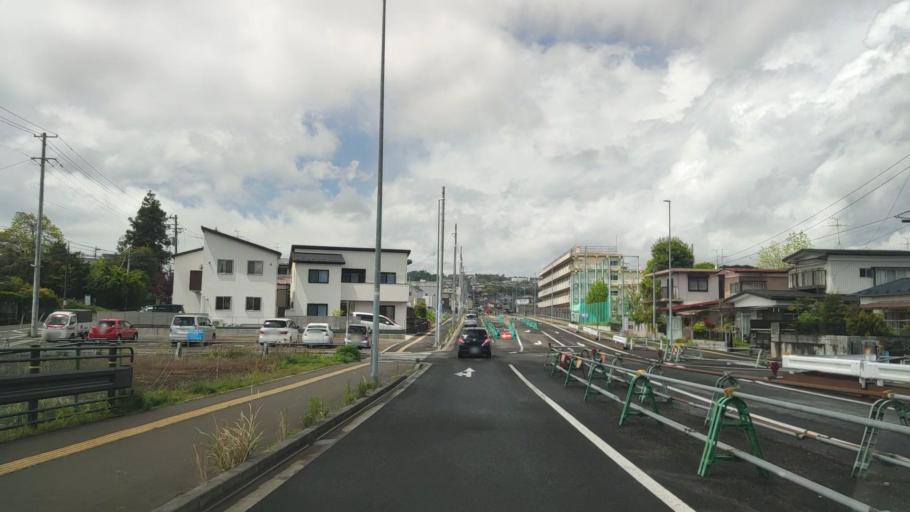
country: JP
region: Miyagi
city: Sendai
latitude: 38.2291
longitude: 140.8575
